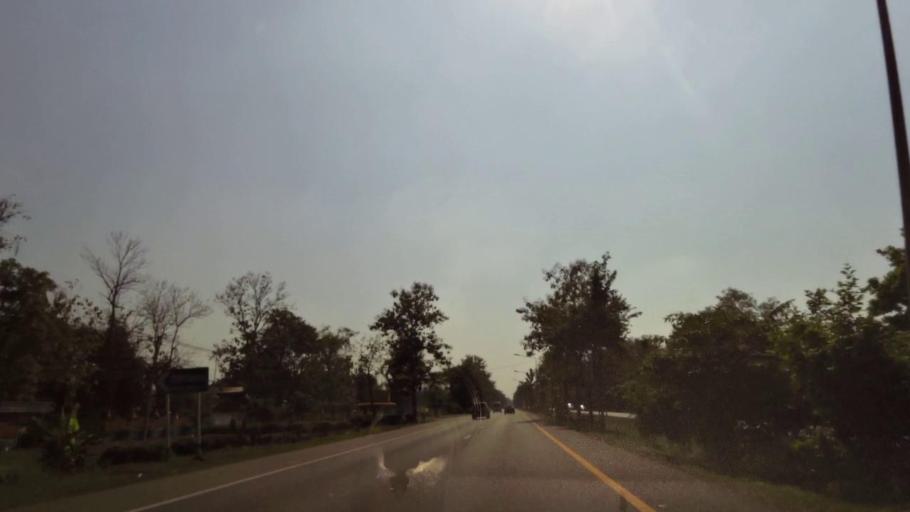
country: TH
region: Phichit
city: Bueng Na Rang
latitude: 16.0754
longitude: 100.1242
